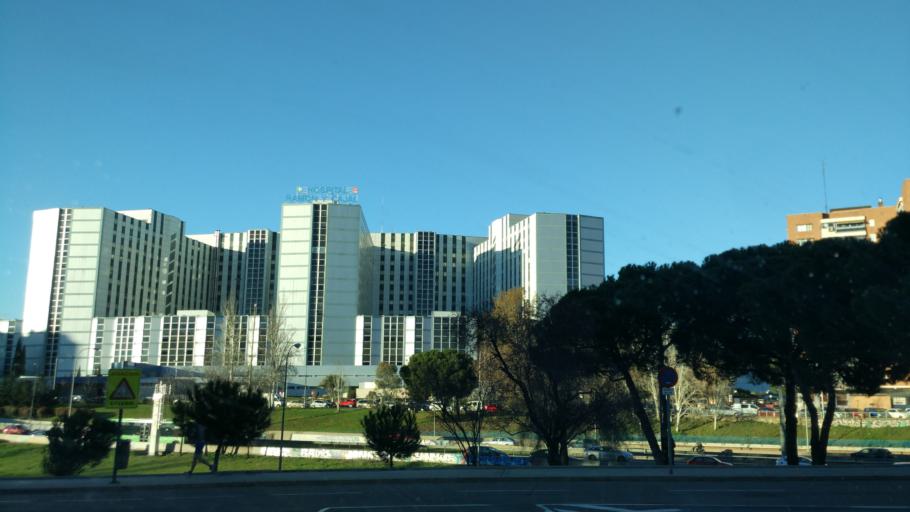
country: ES
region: Madrid
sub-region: Provincia de Madrid
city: Pinar de Chamartin
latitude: 40.4846
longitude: -3.6937
